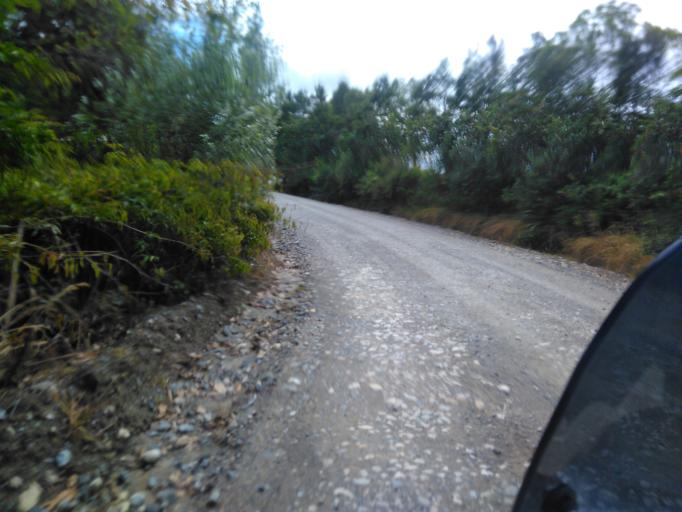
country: NZ
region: Gisborne
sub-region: Gisborne District
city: Gisborne
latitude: -38.2406
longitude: 178.0701
